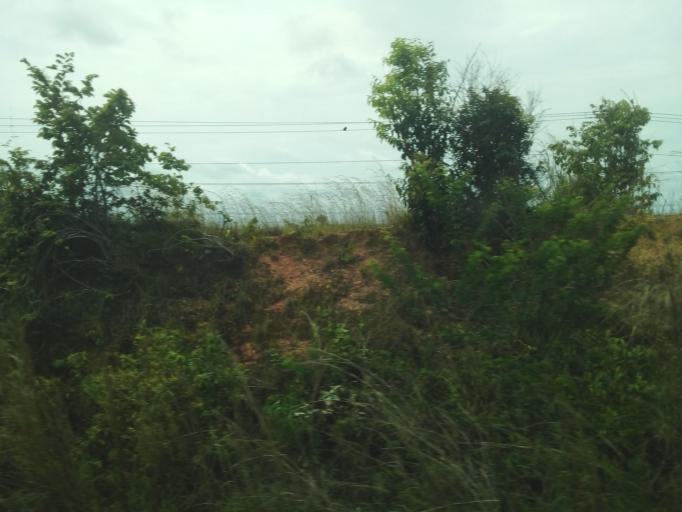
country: BR
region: Maranhao
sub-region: Santa Ines
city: Santa Ines
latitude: -3.6730
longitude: -45.8669
